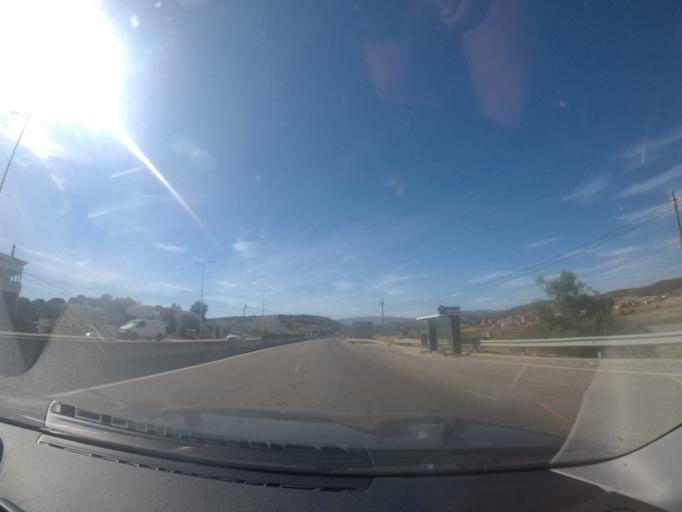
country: PT
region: Faro
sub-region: Portimao
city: Portimao
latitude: 37.1707
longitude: -8.5319
